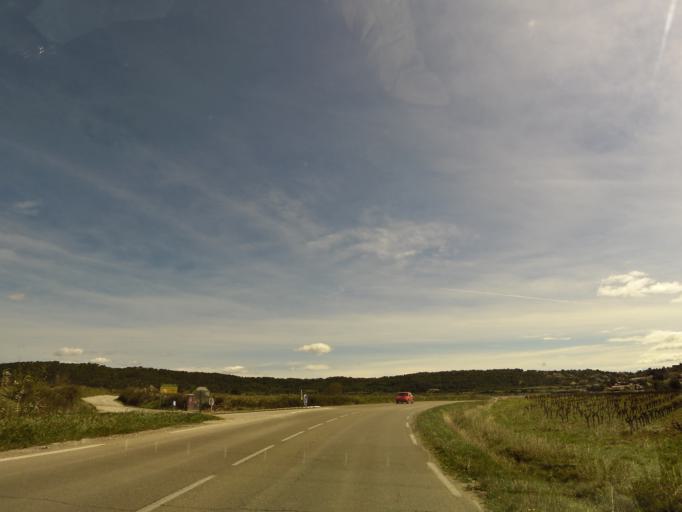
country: FR
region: Languedoc-Roussillon
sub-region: Departement du Gard
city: Langlade
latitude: 43.8158
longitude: 4.2397
